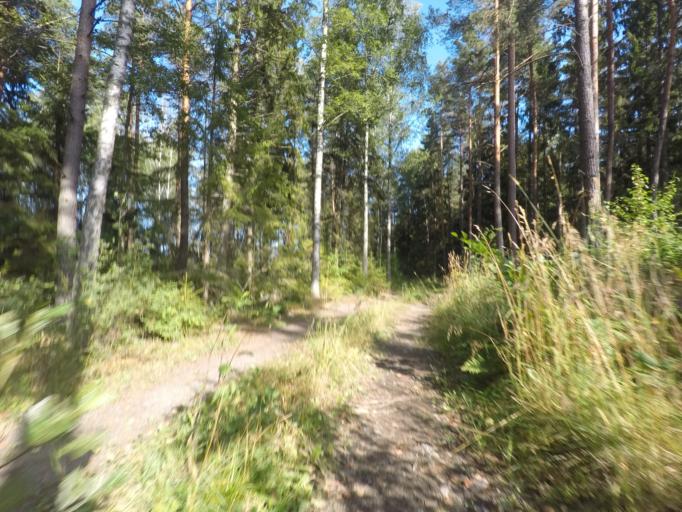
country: SE
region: Soedermanland
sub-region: Eskilstuna Kommun
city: Kvicksund
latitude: 59.4329
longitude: 16.2575
